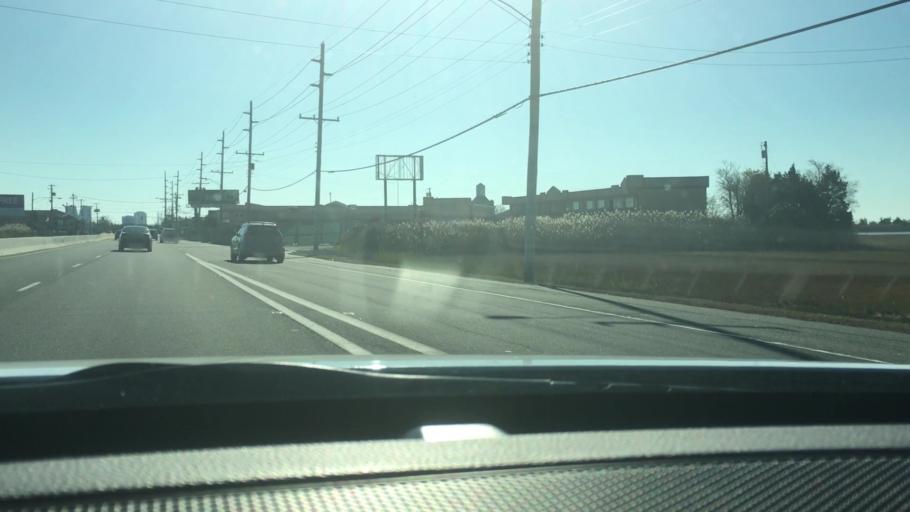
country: US
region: New Jersey
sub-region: Atlantic County
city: Ventnor City
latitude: 39.3729
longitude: -74.4802
